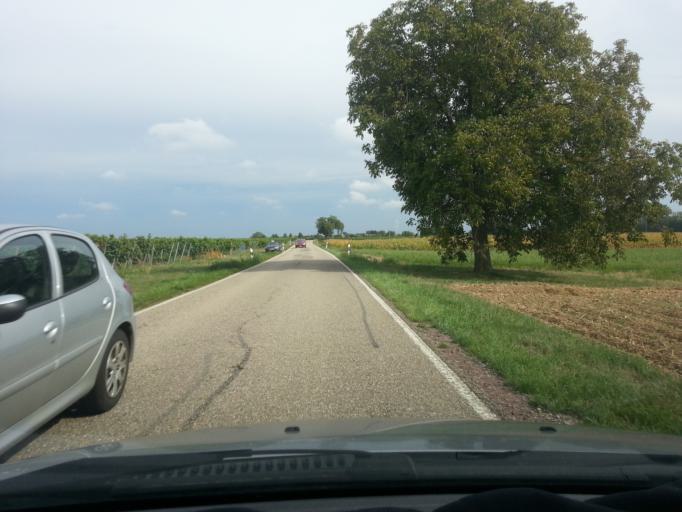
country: DE
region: Rheinland-Pfalz
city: Venningen
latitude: 49.3015
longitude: 8.1923
